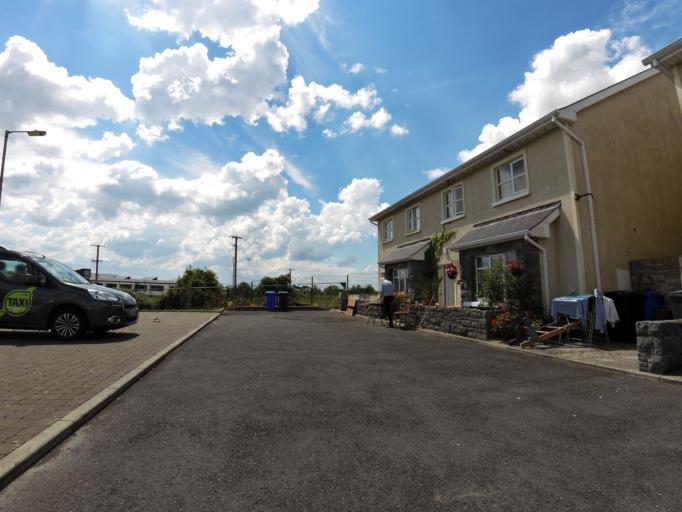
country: IE
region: Connaught
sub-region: County Galway
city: Athenry
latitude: 53.2951
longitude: -8.7540
